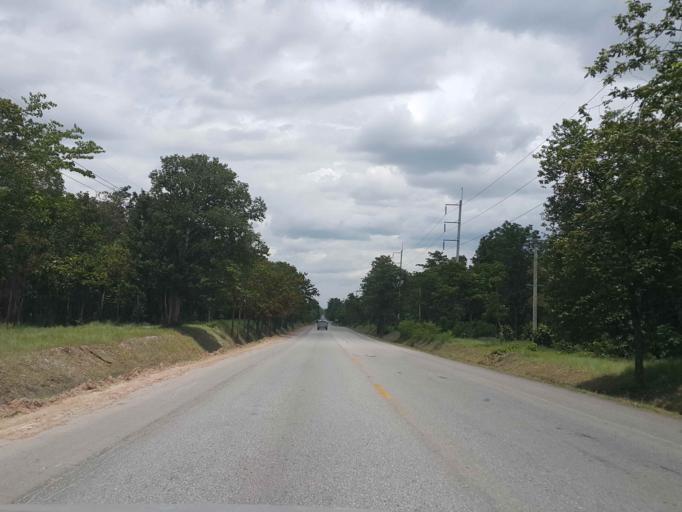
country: TH
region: Chiang Mai
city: Doi Lo
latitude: 18.4155
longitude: 98.8515
